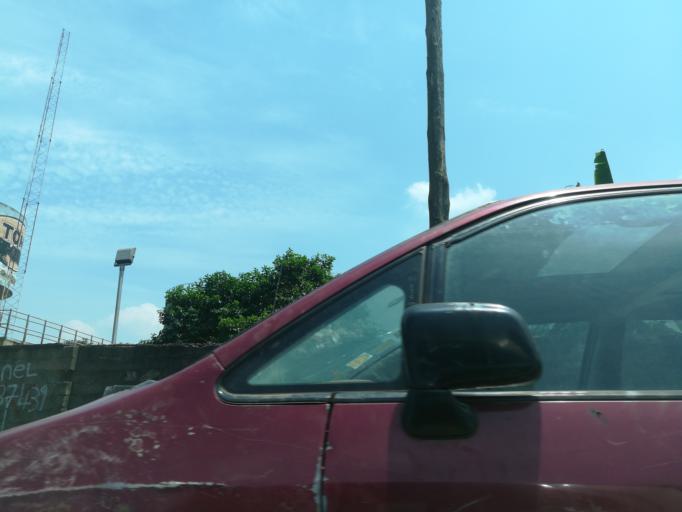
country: NG
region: Lagos
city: Ikorodu
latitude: 6.6228
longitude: 3.4961
